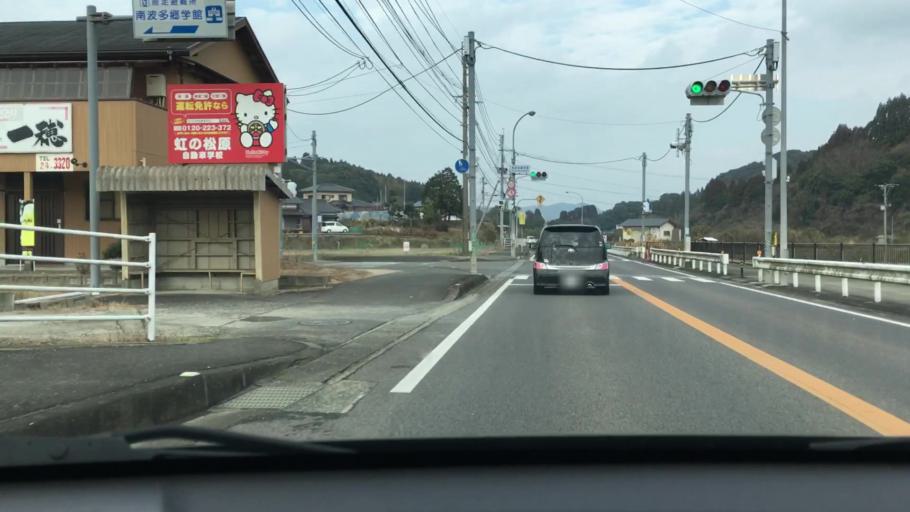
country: JP
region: Saga Prefecture
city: Imaricho-ko
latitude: 33.3168
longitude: 129.9289
